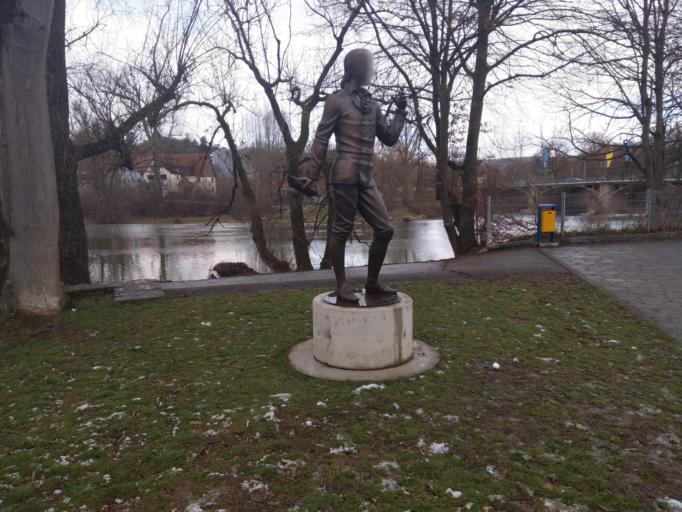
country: DE
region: Baden-Wuerttemberg
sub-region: Regierungsbezirk Stuttgart
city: Nurtingen
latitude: 48.6266
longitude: 9.3341
